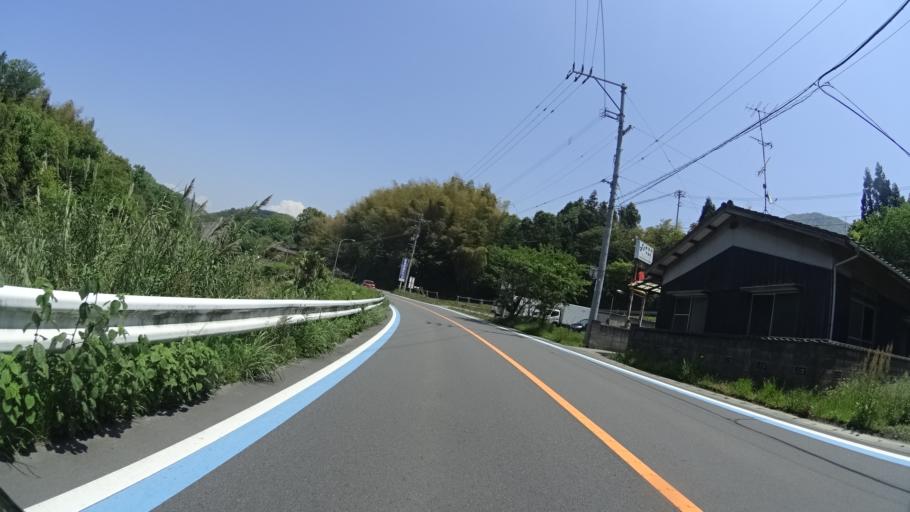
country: JP
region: Ehime
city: Iyo
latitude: 33.7074
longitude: 132.6632
